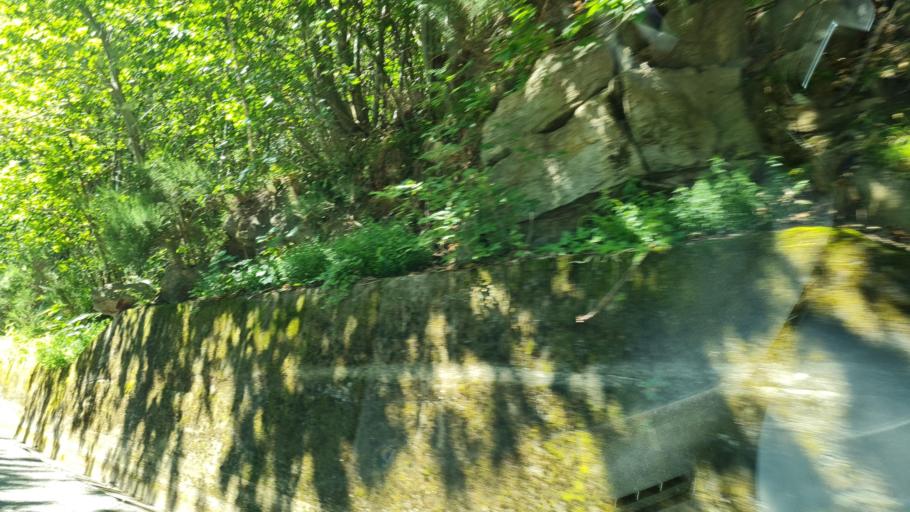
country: IT
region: Piedmont
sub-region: Provincia di Torino
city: Quincinetto
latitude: 45.5567
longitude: 7.8008
